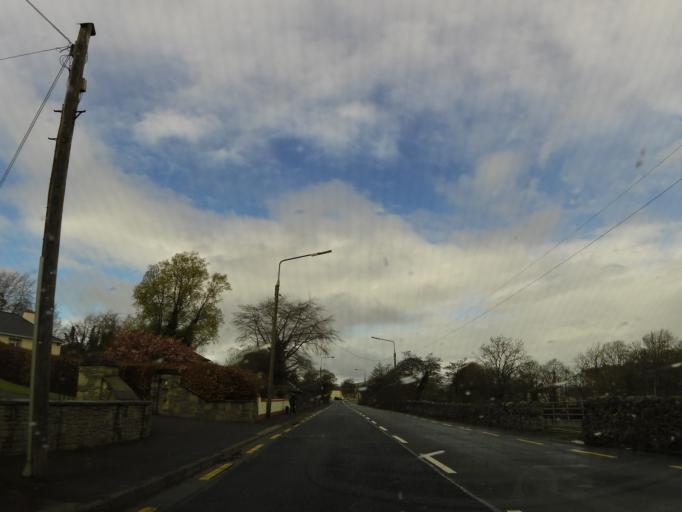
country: IE
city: Ballisodare
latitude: 54.2077
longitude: -8.5071
